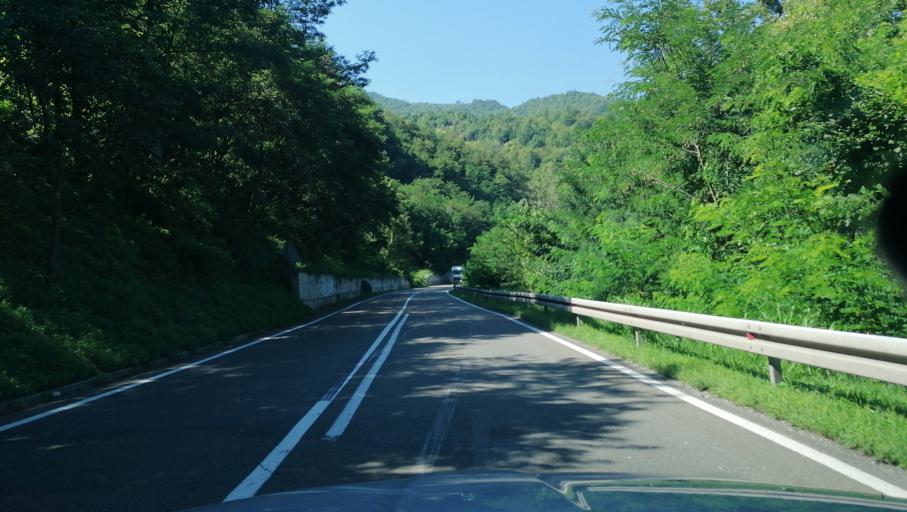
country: RS
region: Central Serbia
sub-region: Raski Okrug
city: Kraljevo
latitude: 43.6119
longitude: 20.5484
